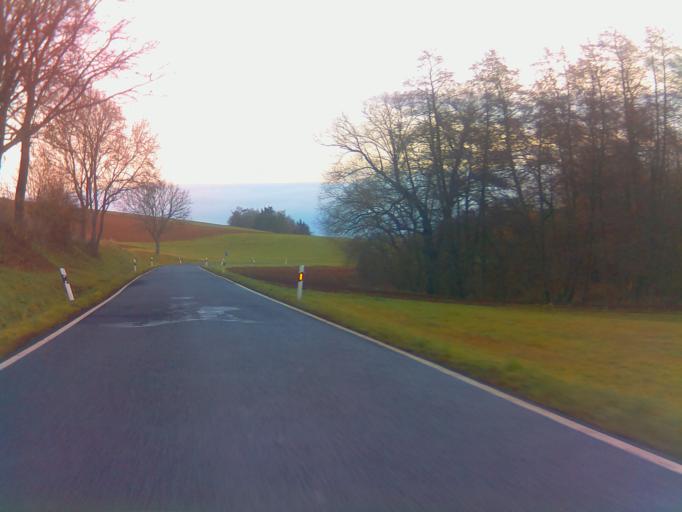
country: DE
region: Rheinland-Pfalz
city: Wendelsheim
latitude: 49.7544
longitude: 7.9849
